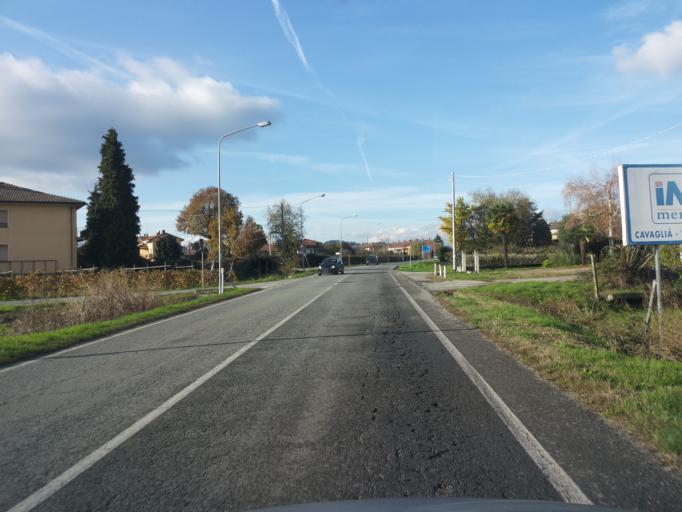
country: IT
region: Piedmont
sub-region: Provincia di Vercelli
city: Alice Castello
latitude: 45.3693
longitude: 8.0803
